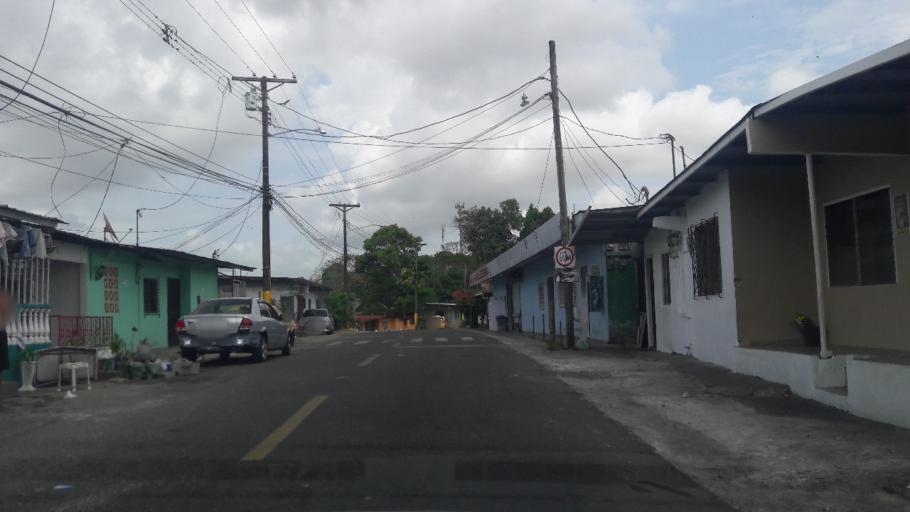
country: PA
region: Panama
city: Alcalde Diaz
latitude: 9.1238
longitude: -79.5571
